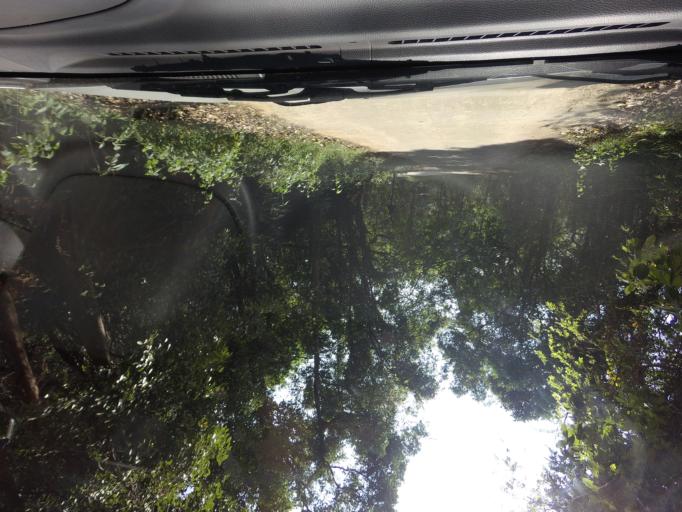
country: IN
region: Karnataka
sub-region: Kodagu
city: Somvarpet
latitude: 12.7032
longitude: 75.6419
